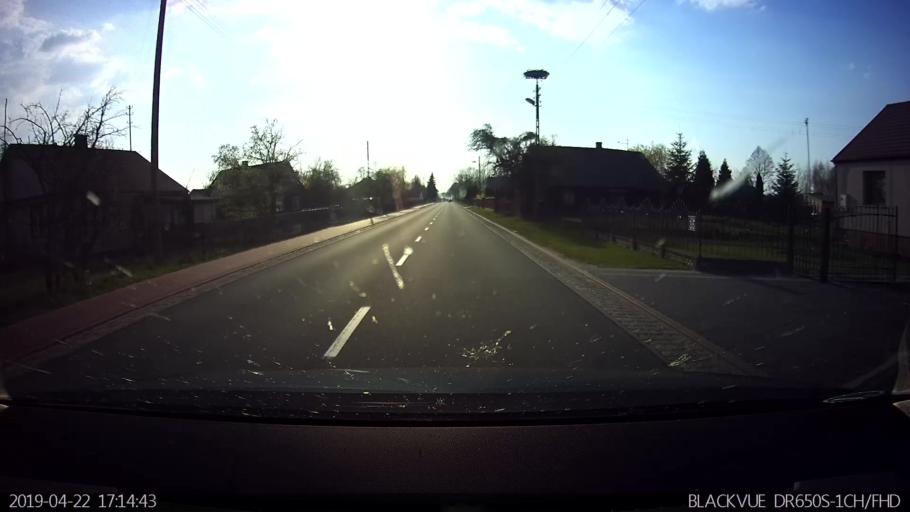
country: PL
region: Masovian Voivodeship
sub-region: Powiat sokolowski
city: Jablonna Lacka
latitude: 52.4016
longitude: 22.4987
